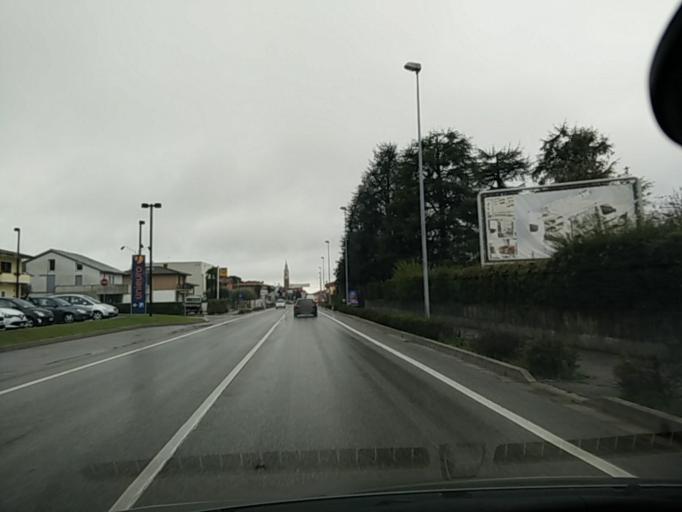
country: IT
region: Veneto
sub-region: Provincia di Vicenza
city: San Zeno-San Giuseppe
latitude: 45.7316
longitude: 11.7608
